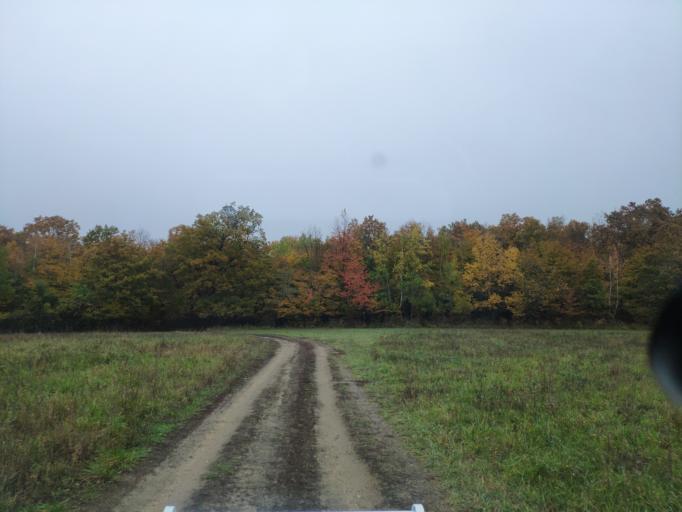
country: SK
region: Kosicky
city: Moldava nad Bodvou
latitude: 48.7146
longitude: 21.0126
